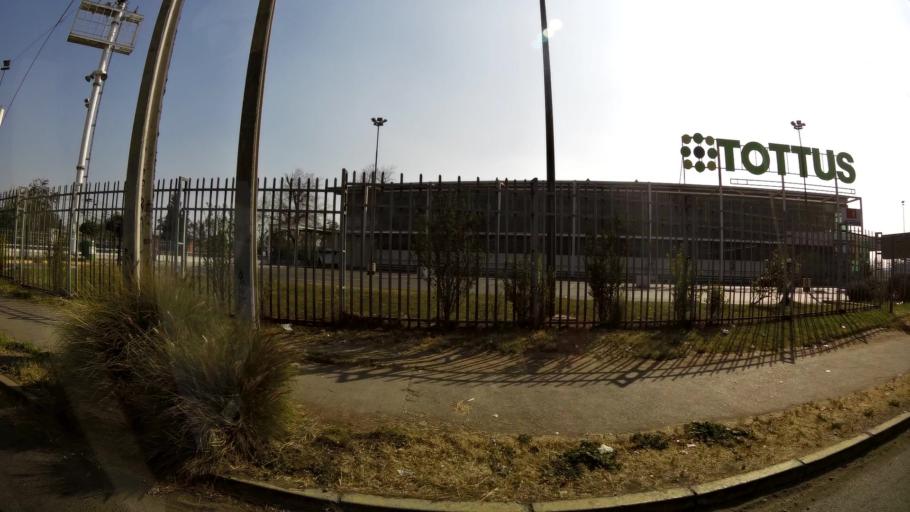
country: CL
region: Santiago Metropolitan
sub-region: Provincia de Santiago
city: Santiago
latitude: -33.3718
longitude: -70.6712
